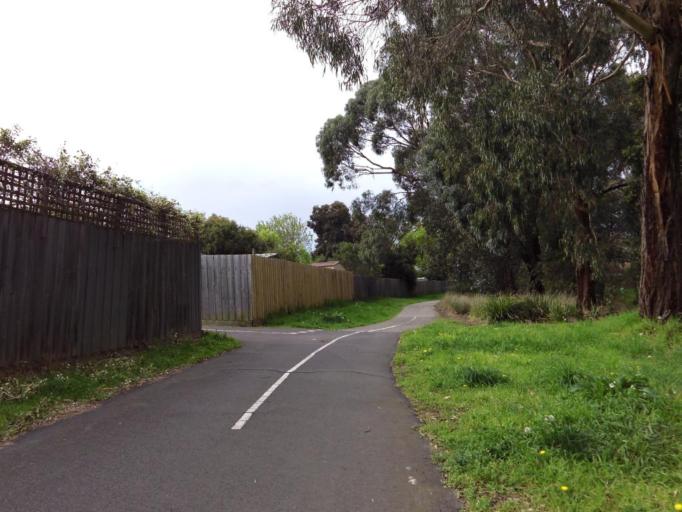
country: AU
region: Victoria
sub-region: Maroondah
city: Croydon Hills
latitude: -37.7882
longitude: 145.2580
